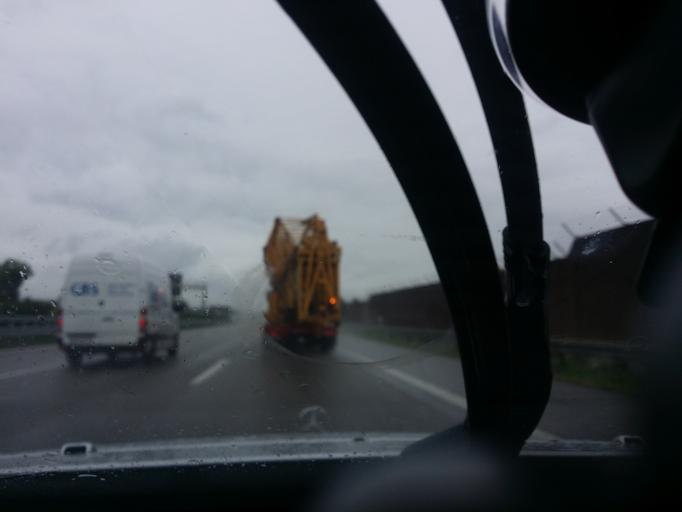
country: DE
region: Baden-Wuerttemberg
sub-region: Regierungsbezirk Stuttgart
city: Filderstadt
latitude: 48.6939
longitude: 9.2251
